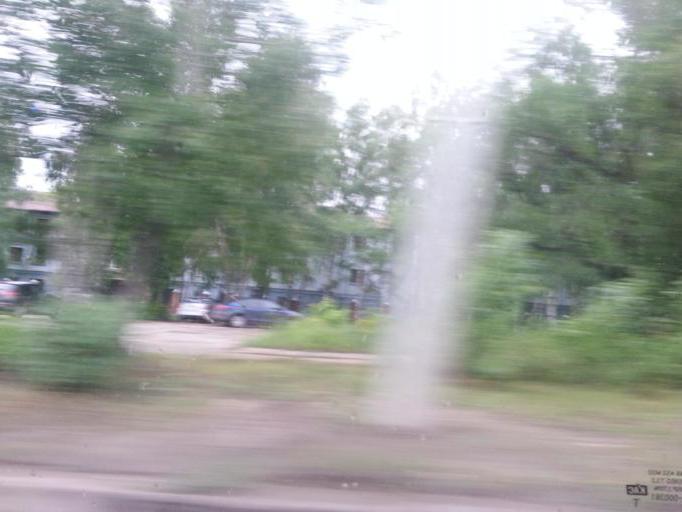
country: RU
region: Tatarstan
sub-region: Gorod Kazan'
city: Kazan
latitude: 55.7643
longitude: 49.2015
